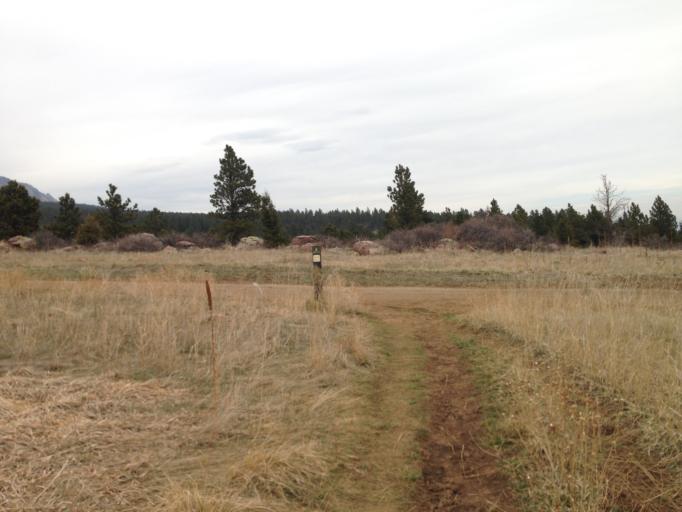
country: US
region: Colorado
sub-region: Boulder County
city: Boulder
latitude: 39.9456
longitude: -105.2712
